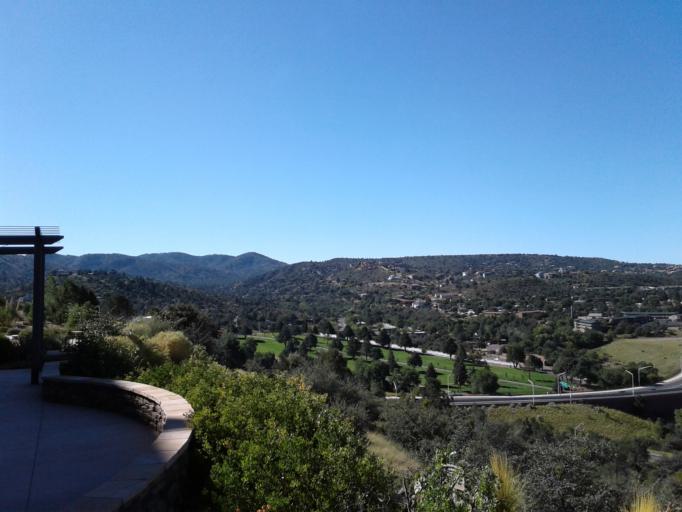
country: US
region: Arizona
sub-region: Yavapai County
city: Prescott
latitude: 34.5507
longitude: -112.4474
